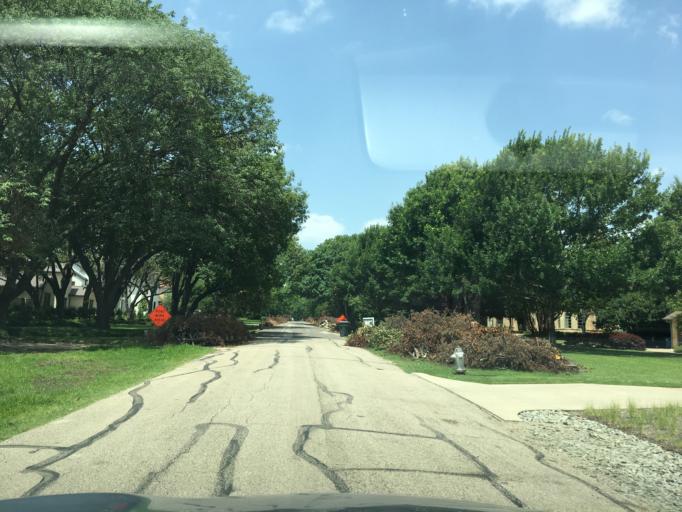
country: US
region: Texas
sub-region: Dallas County
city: University Park
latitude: 32.9054
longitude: -96.7924
